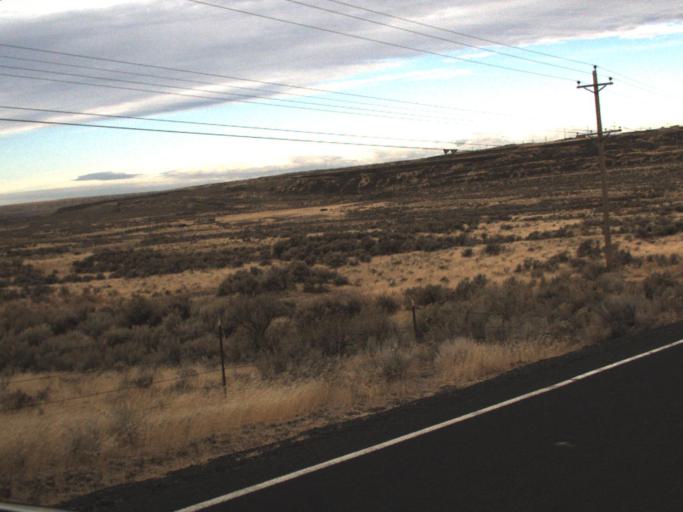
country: US
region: Washington
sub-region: Adams County
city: Ritzville
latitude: 47.4618
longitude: -118.7620
